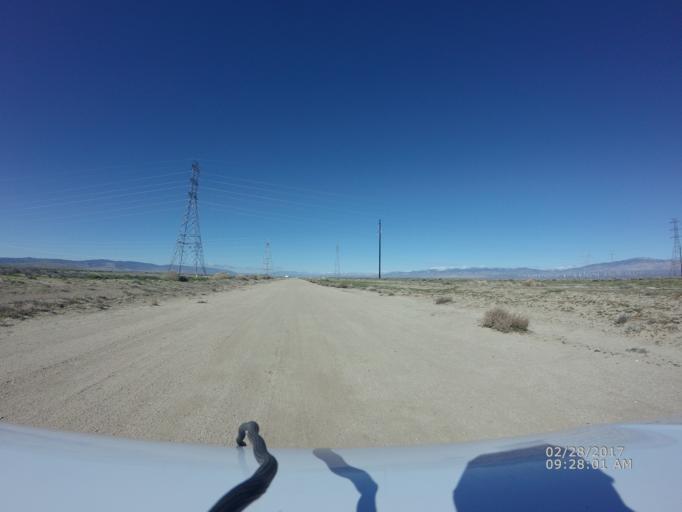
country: US
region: California
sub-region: Kern County
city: Rosamond
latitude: 34.8049
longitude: -118.3407
